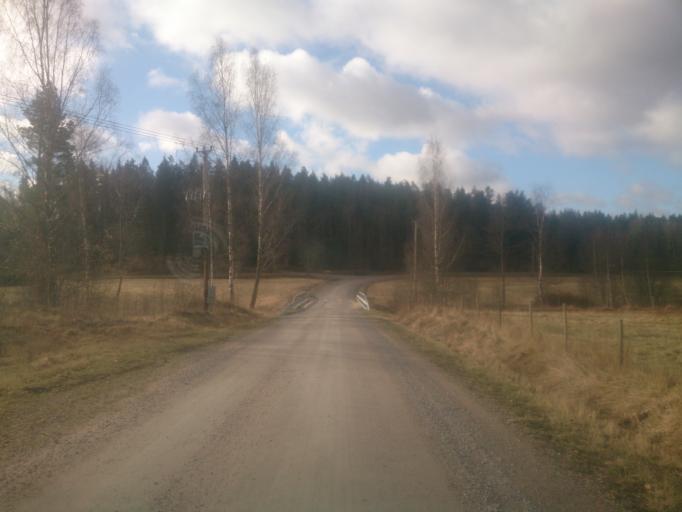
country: SE
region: OEstergoetland
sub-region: Atvidabergs Kommun
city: Atvidaberg
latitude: 58.2092
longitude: 16.1670
